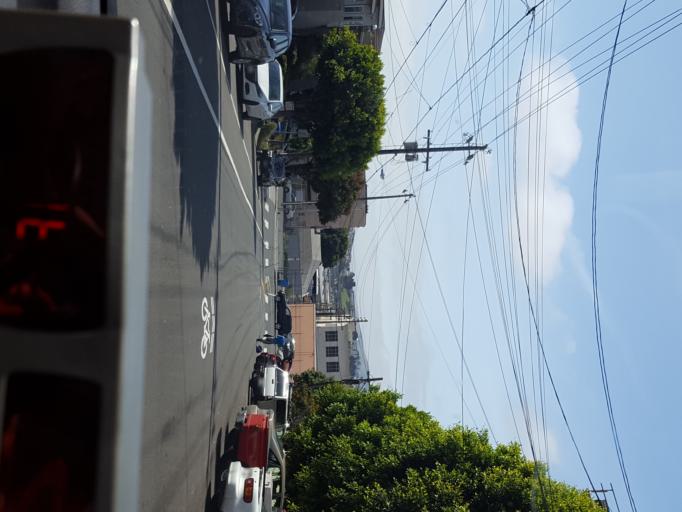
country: US
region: California
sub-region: San Francisco County
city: San Francisco
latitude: 37.7514
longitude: -122.4022
